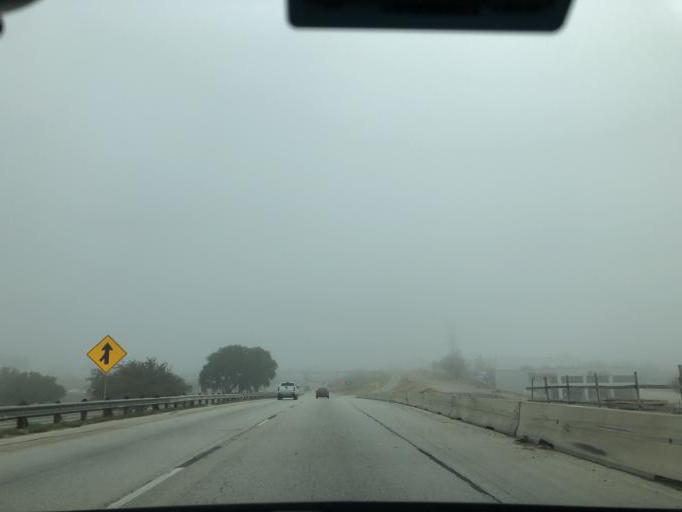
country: US
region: Texas
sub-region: Tarrant County
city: Richland Hills
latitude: 32.8054
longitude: -97.2111
